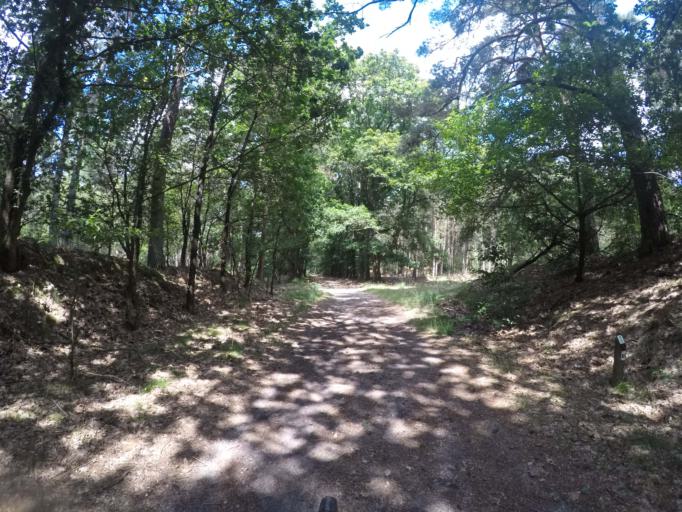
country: NL
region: Drenthe
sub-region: Gemeente Westerveld
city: Dwingeloo
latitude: 52.8780
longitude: 6.3073
